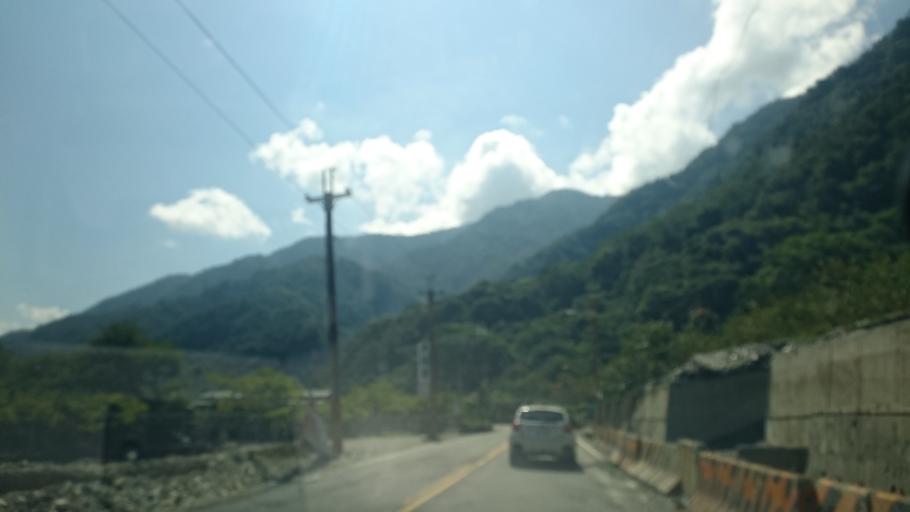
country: TW
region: Taiwan
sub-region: Nantou
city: Puli
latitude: 23.9952
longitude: 121.0723
